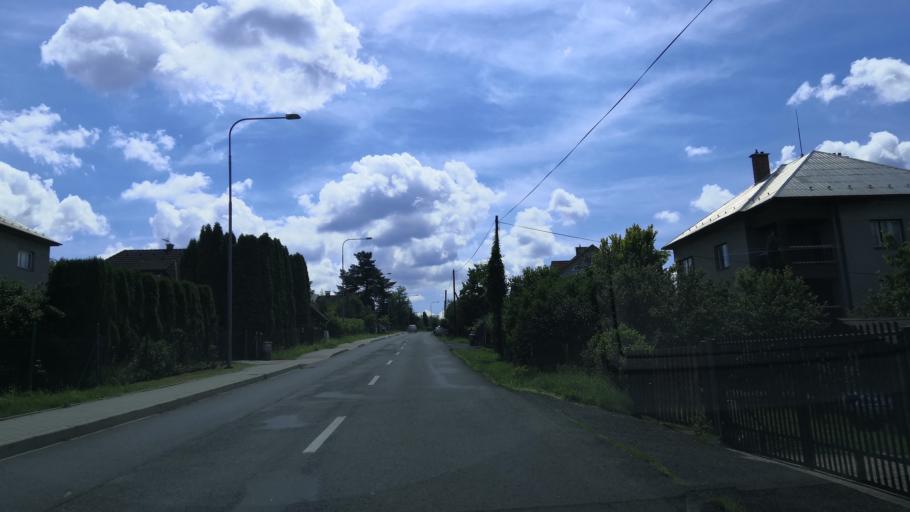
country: CZ
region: Zlin
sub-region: Okres Vsetin
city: Roznov pod Radhostem
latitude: 49.4523
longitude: 18.1432
